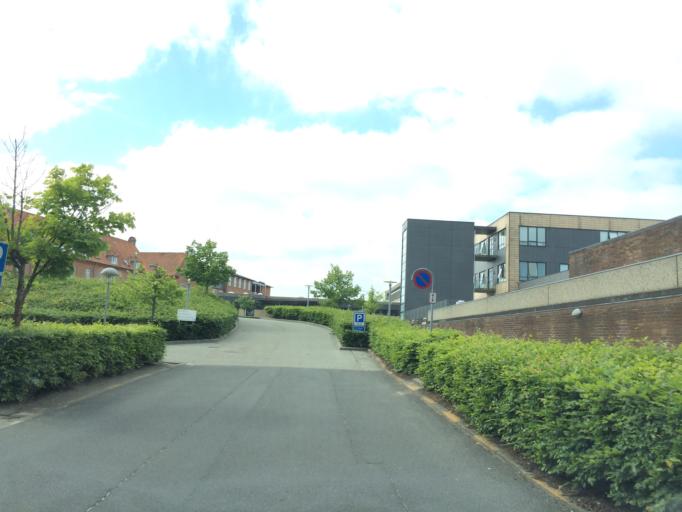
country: DK
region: Central Jutland
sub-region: Herning Kommune
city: Herning
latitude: 56.1407
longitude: 8.9715
